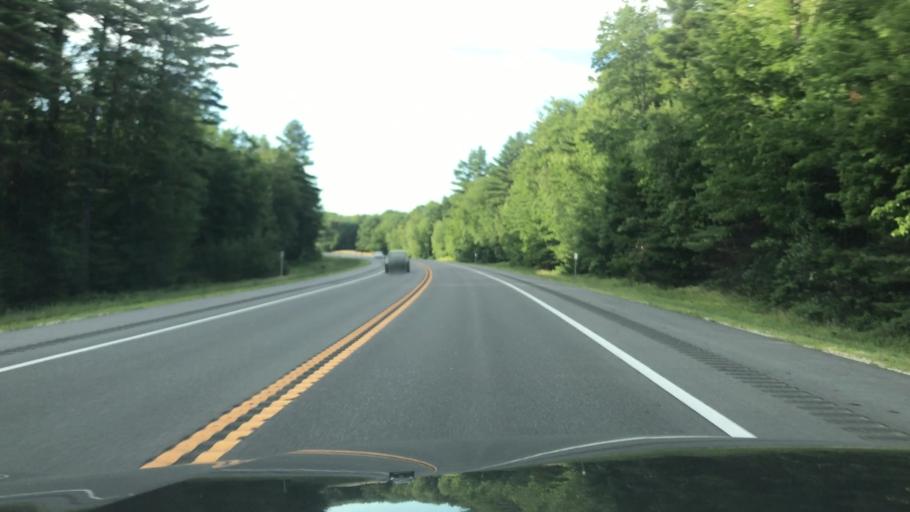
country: US
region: New Hampshire
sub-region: Strafford County
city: Farmington
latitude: 43.4549
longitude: -70.9939
